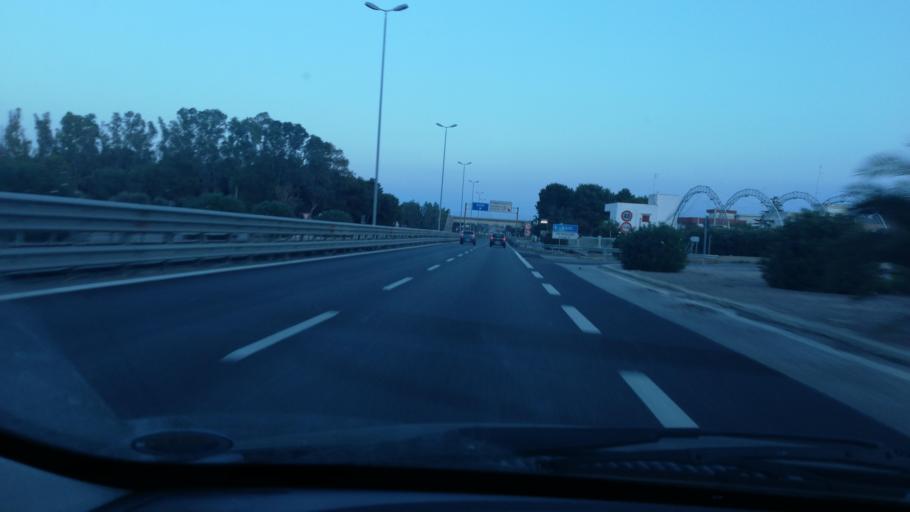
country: IT
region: Apulia
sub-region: Provincia di Bari
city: San Paolo
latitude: 41.1471
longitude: 16.7892
